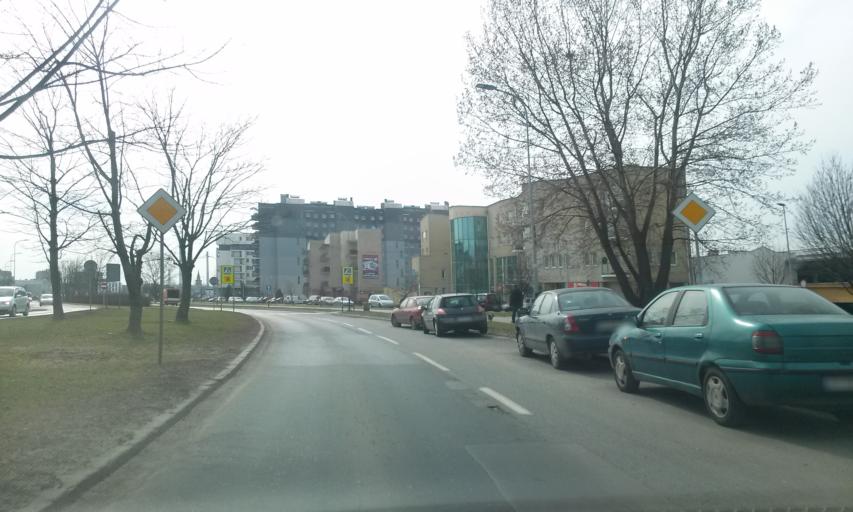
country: PL
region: Lesser Poland Voivodeship
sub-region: Krakow
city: Krakow
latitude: 50.0820
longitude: 20.0157
